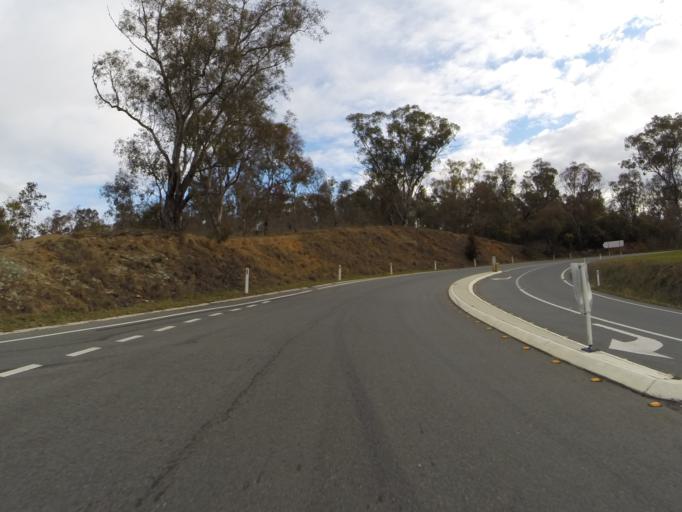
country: AU
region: Australian Capital Territory
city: Macquarie
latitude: -35.3209
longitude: 148.9558
